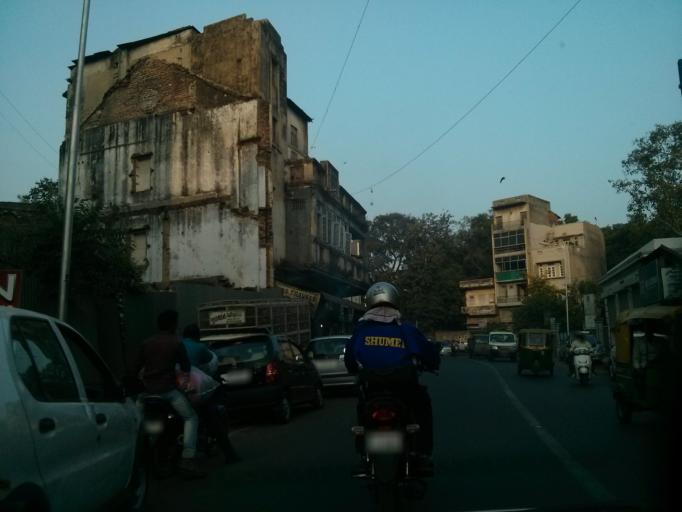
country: IN
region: Gujarat
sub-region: Ahmadabad
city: Ahmedabad
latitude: 23.0290
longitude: 72.5817
